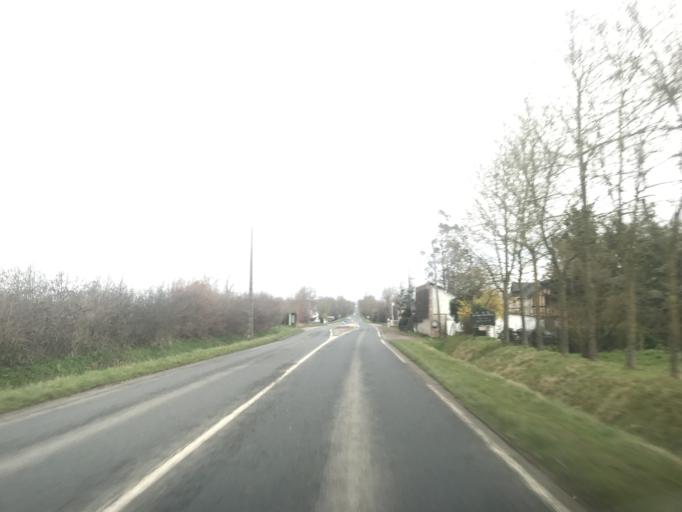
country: FR
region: Lower Normandy
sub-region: Departement du Calvados
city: Troarn
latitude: 49.1991
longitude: -0.1313
